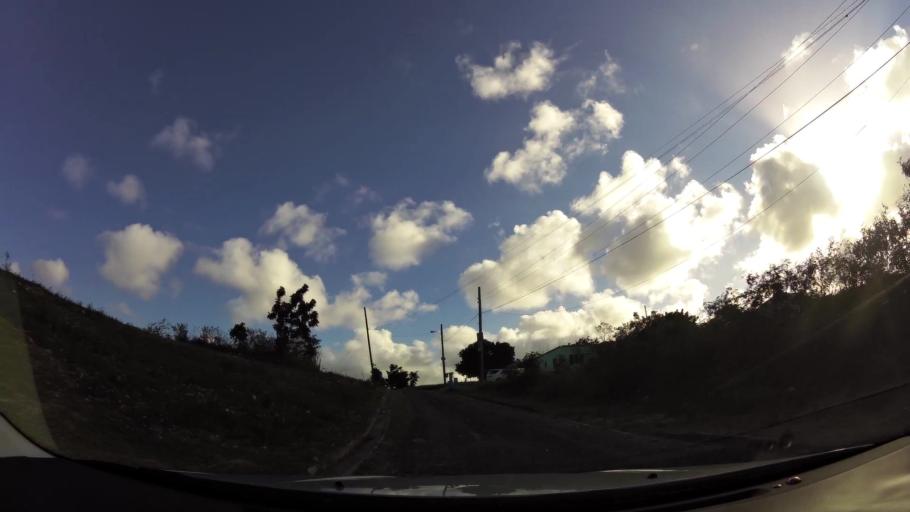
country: AG
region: Saint George
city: Piggotts
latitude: 17.1225
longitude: -61.7919
